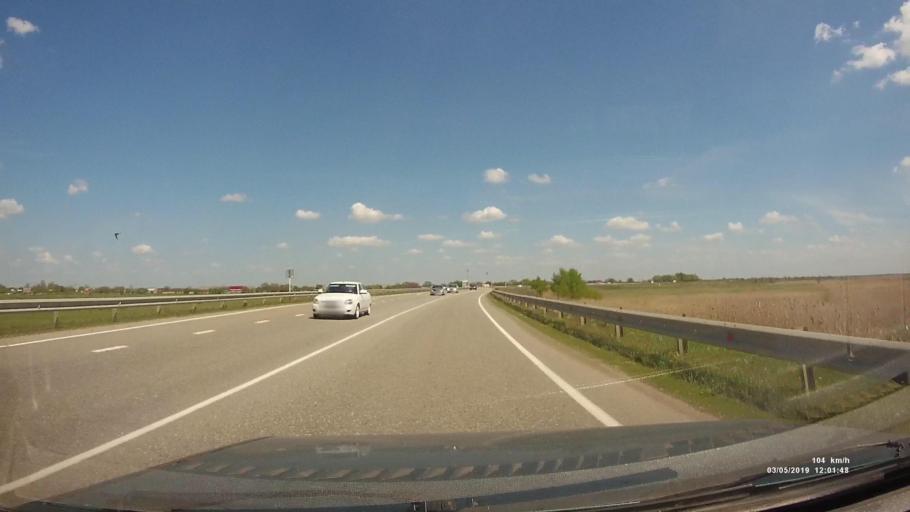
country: RU
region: Rostov
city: Bagayevskaya
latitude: 47.2678
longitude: 40.3547
